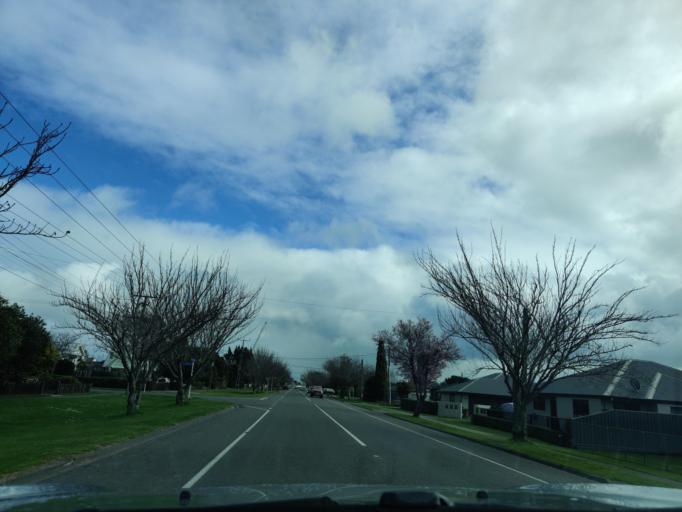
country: NZ
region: Hawke's Bay
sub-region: Hastings District
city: Hastings
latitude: -39.6712
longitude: 176.8715
